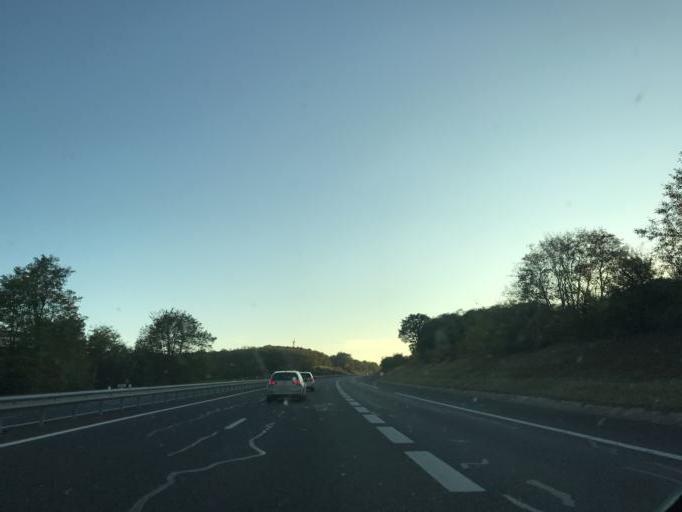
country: FR
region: Bourgogne
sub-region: Departement de l'Yonne
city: Saint-Martin-du-Tertre
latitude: 48.2164
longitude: 3.2338
